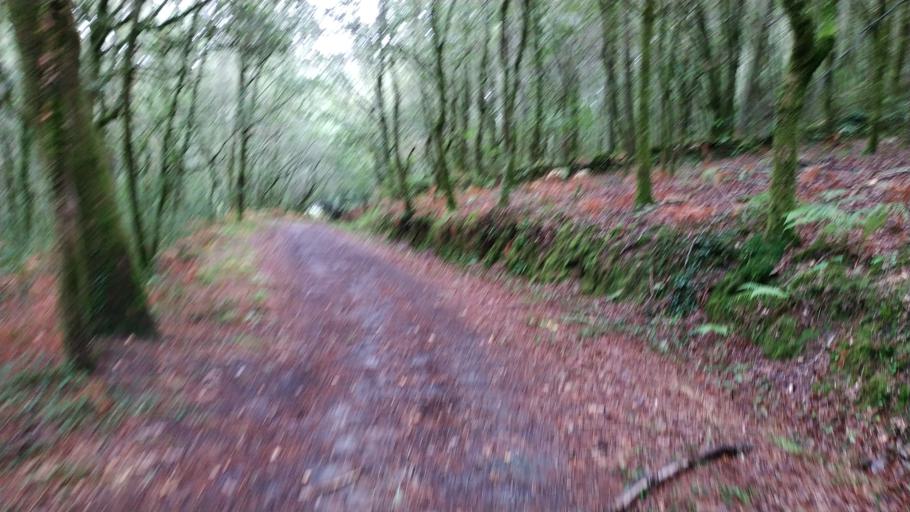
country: ES
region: Galicia
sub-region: Provincia da Coruna
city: Negreira
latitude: 42.9121
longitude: -8.7510
